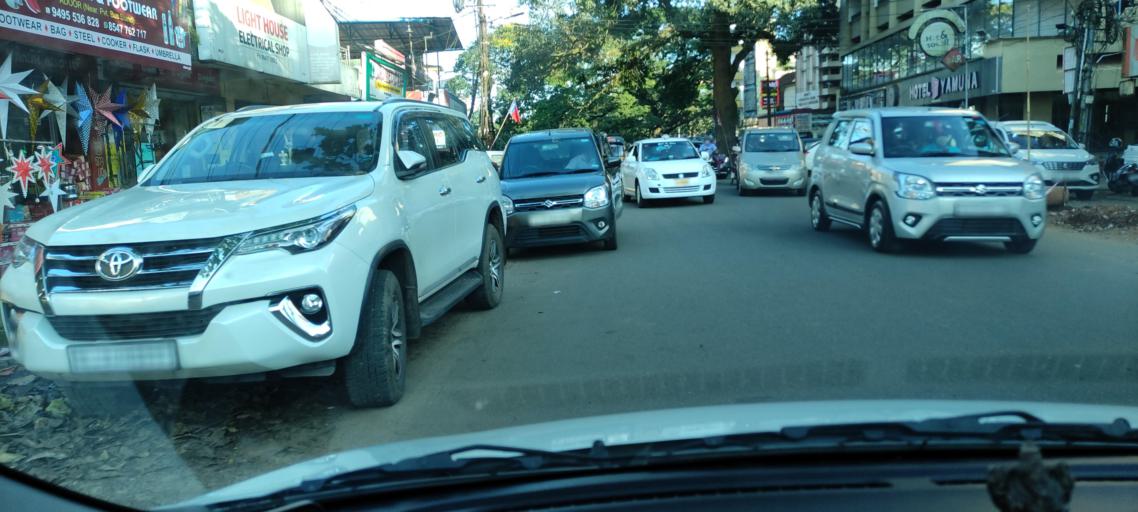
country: IN
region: Kerala
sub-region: Pattanamtitta
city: Adur
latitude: 9.1569
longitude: 76.7297
